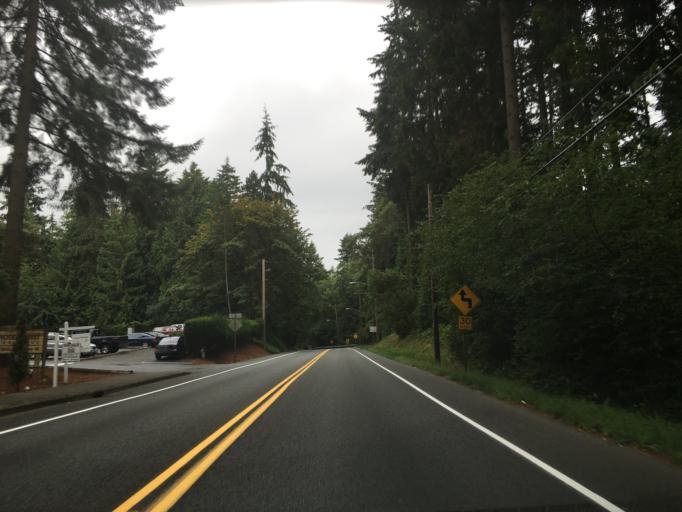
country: US
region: Washington
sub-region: King County
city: Inglewood-Finn Hill
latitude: 47.7271
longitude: -122.2439
